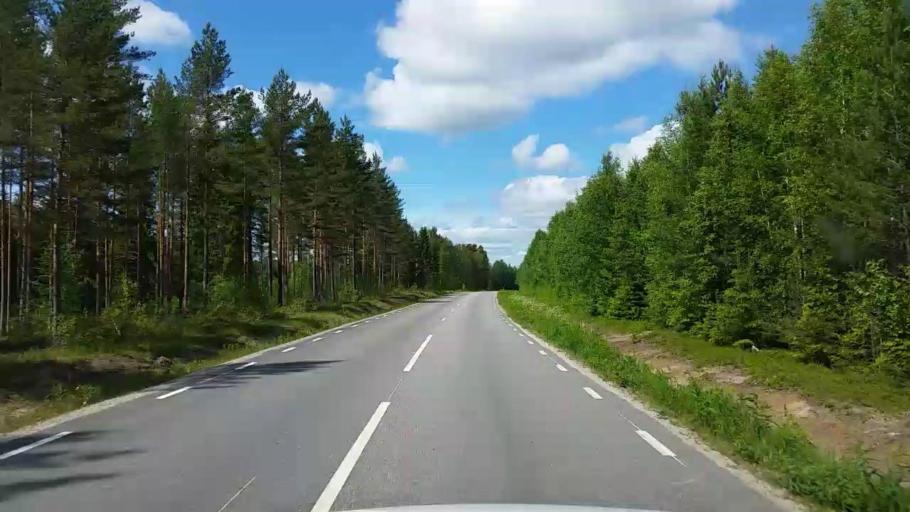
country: SE
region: Gaevleborg
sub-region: Ovanakers Kommun
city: Alfta
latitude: 61.2651
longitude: 16.1215
